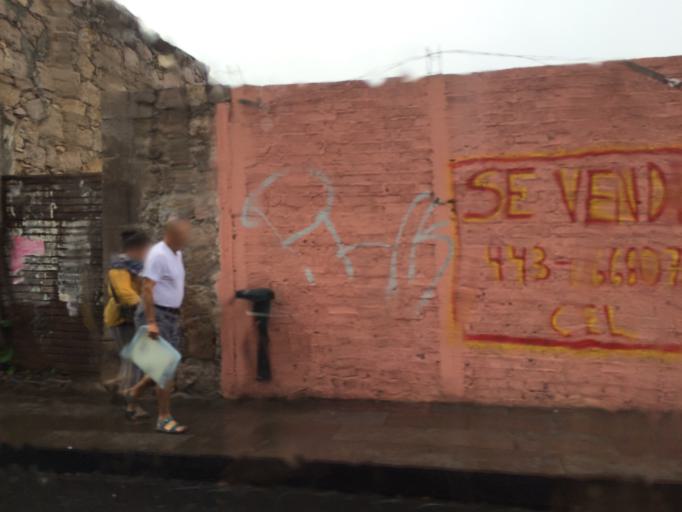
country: MX
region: Michoacan
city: Morelia
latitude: 19.7031
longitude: -101.1987
